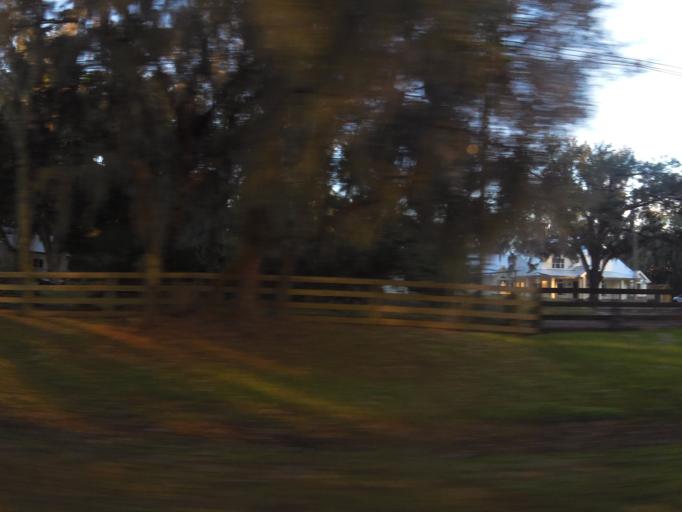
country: US
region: Florida
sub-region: Clay County
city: Green Cove Springs
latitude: 29.9216
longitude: -81.5938
